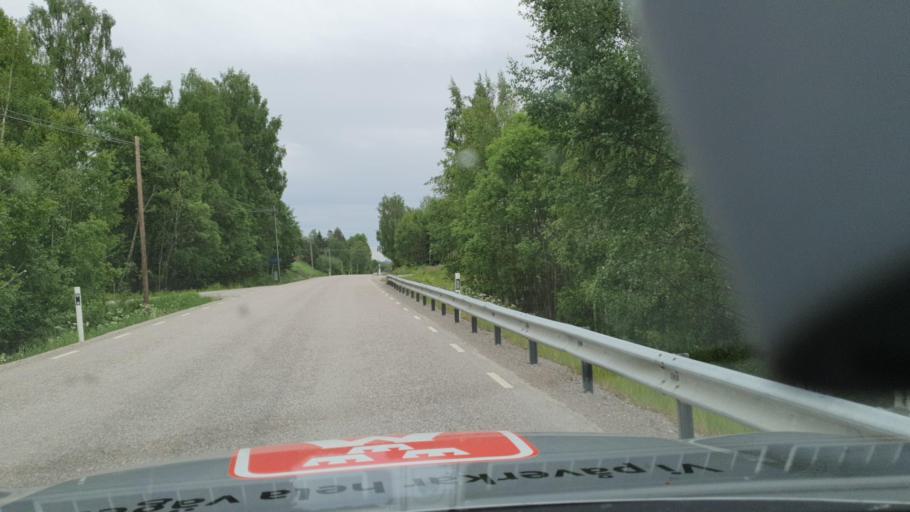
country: SE
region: Vaesternorrland
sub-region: Kramfors Kommun
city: Kramfors
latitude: 62.9410
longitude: 17.9052
